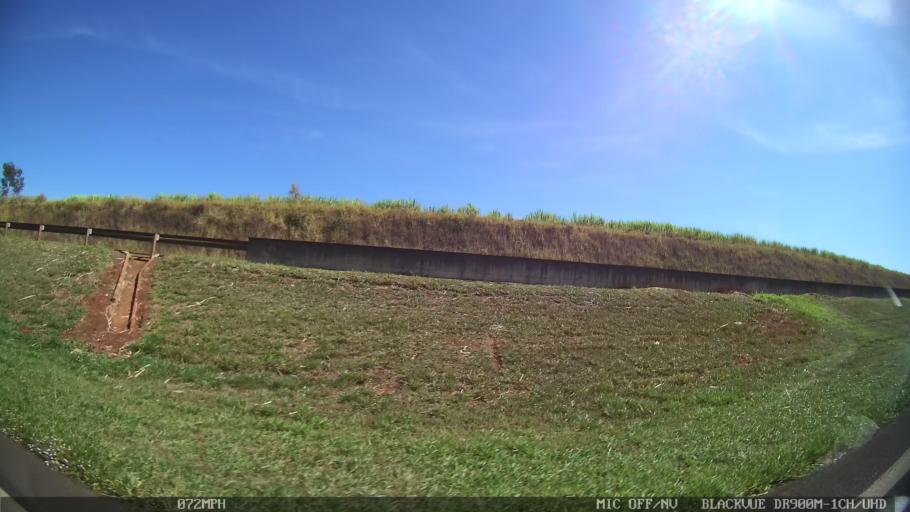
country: BR
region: Sao Paulo
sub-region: Sao Simao
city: Sao Simao
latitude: -21.4982
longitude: -47.6417
